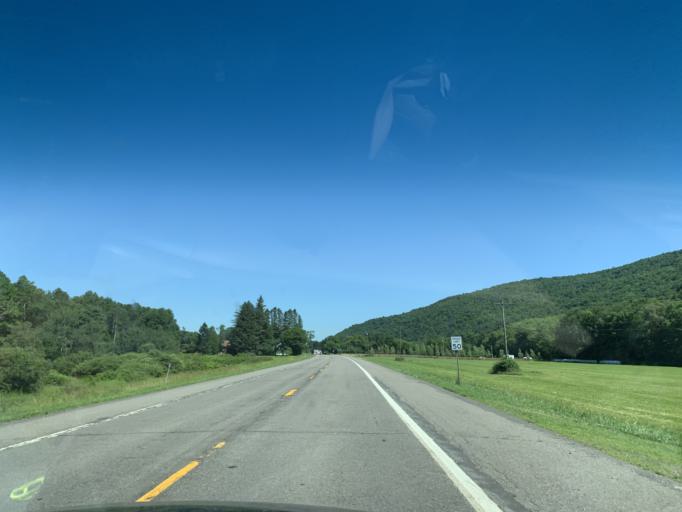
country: US
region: New York
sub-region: Delaware County
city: Sidney
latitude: 42.4408
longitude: -75.3873
